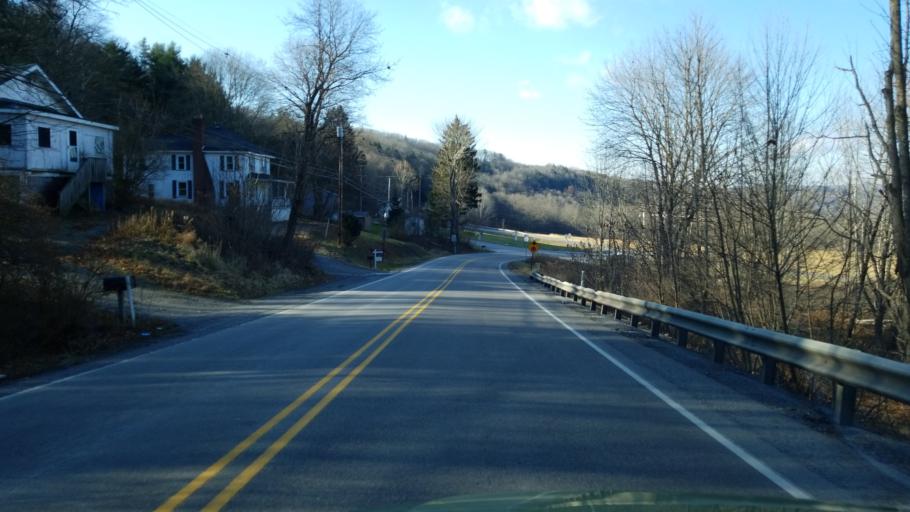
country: US
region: Pennsylvania
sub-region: Clearfield County
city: Clearfield
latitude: 41.0031
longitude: -78.4251
